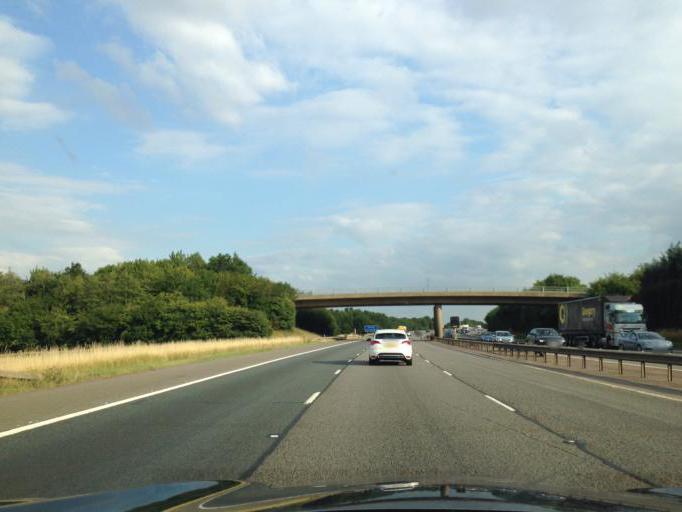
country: GB
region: England
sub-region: Warwickshire
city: Harbury
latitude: 52.1882
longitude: -1.4520
